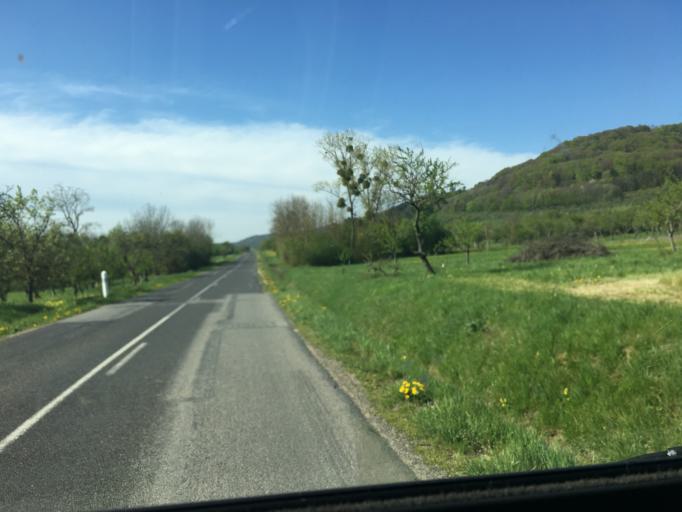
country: FR
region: Lorraine
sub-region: Departement de la Meuse
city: Vigneulles-les-Hattonchatel
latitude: 48.9271
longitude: 5.6899
